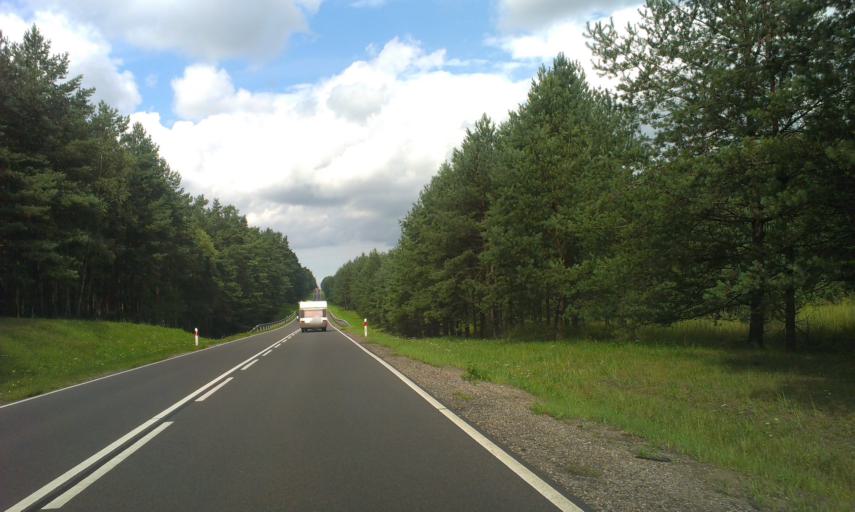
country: PL
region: West Pomeranian Voivodeship
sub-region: Powiat koszalinski
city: Sianow
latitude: 54.1046
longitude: 16.3420
